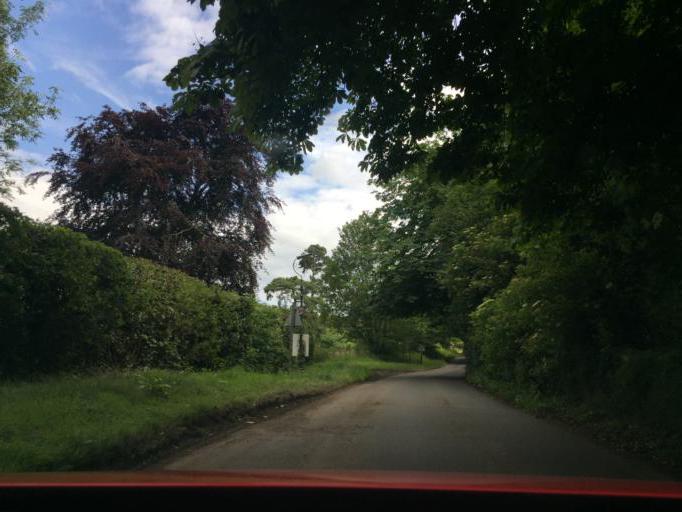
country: GB
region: England
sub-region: Hertfordshire
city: Knebworth
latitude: 51.8713
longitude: -0.2115
